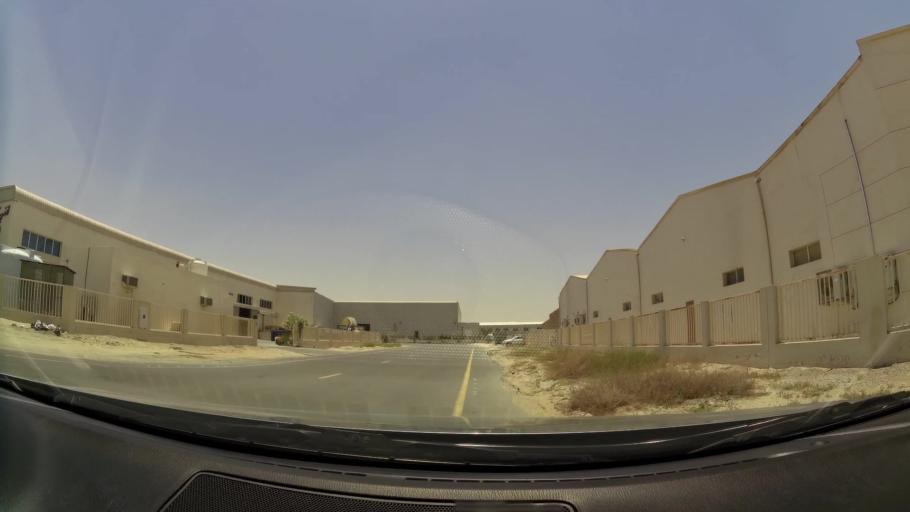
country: AE
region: Dubai
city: Dubai
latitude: 24.9799
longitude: 55.1743
